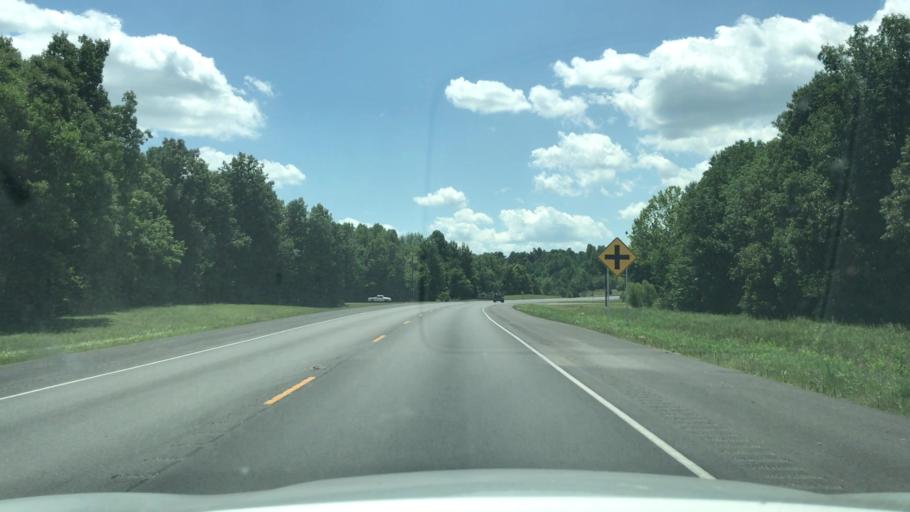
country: US
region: Kentucky
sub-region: Muhlenberg County
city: Greenville
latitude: 37.2066
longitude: -87.1954
